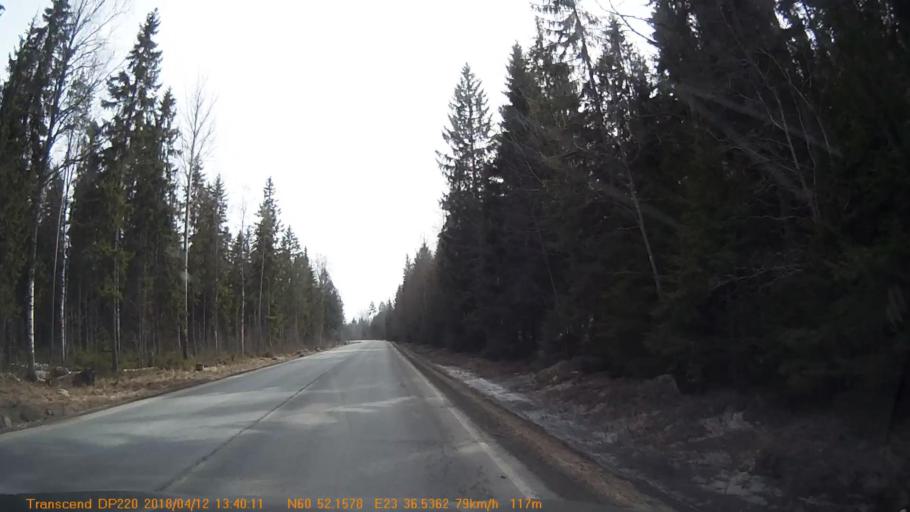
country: FI
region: Haeme
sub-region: Forssa
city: Forssa
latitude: 60.8687
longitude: 23.6093
